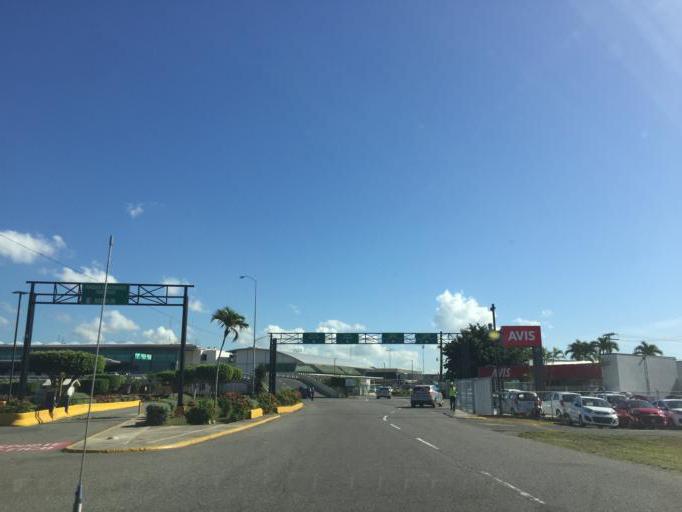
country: DO
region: Santo Domingo
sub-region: Santo Domingo
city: Boca Chica
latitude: 18.4285
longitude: -69.6777
